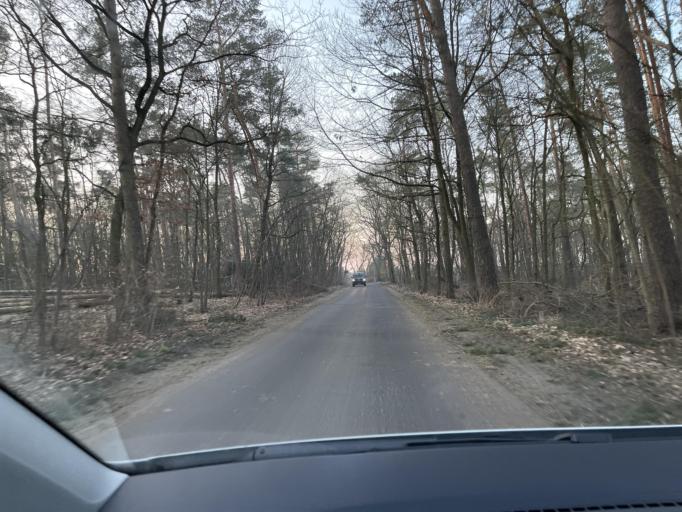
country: DE
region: Brandenburg
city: Roskow
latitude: 52.3932
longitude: 12.6922
